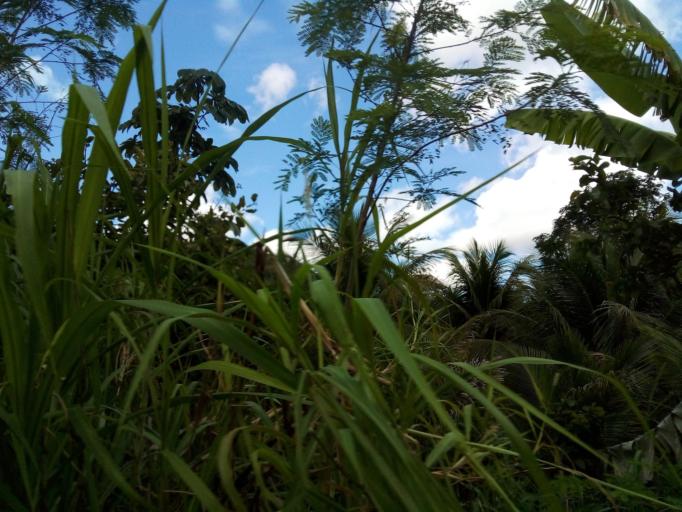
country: BR
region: Espirito Santo
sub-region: Ibiracu
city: Ibiracu
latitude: -19.8702
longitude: -40.3613
